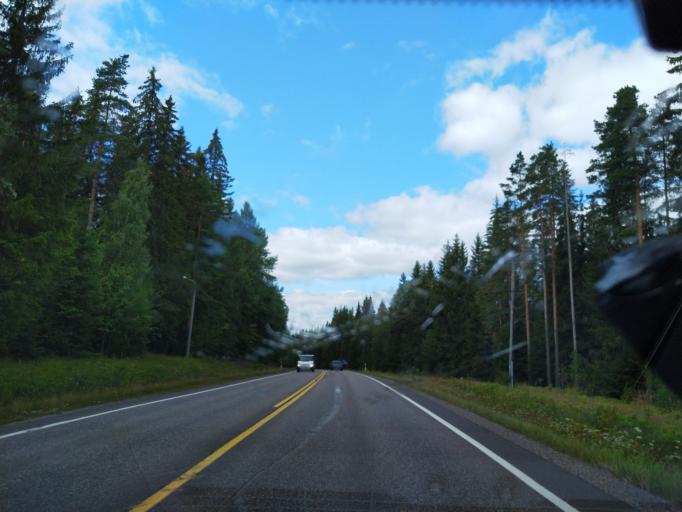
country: FI
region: Haeme
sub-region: Haemeenlinna
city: Renko
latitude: 60.7598
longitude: 24.2914
